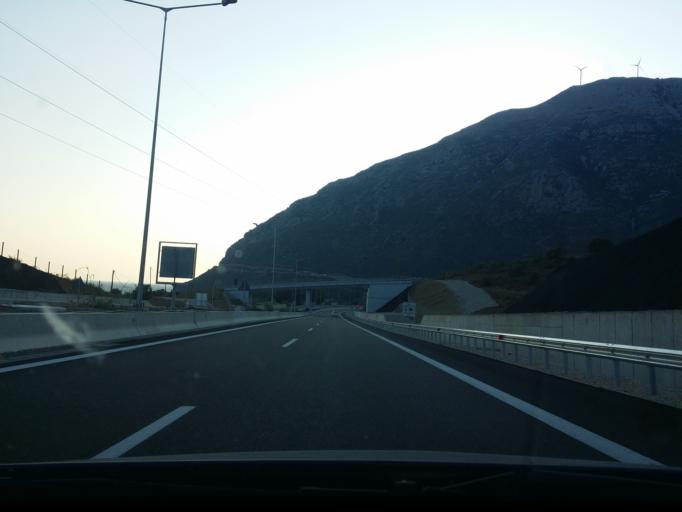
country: GR
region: West Greece
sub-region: Nomos Aitolias kai Akarnanias
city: Antirrio
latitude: 38.3540
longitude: 21.7137
